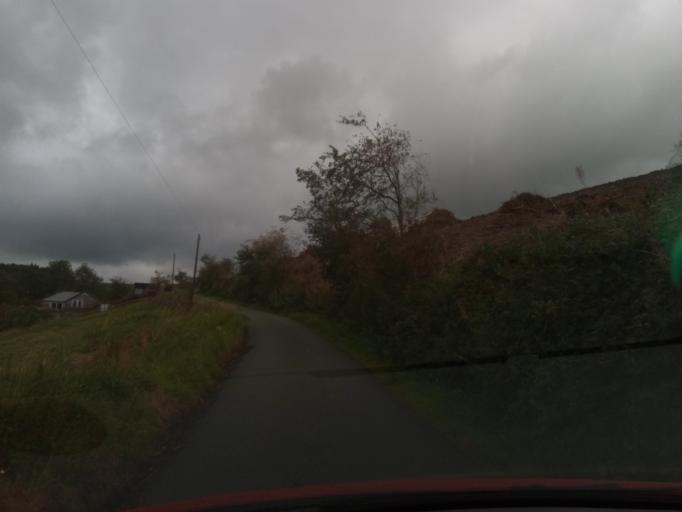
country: GB
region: Scotland
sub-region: The Scottish Borders
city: Coldstream
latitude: 55.5452
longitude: -2.2713
